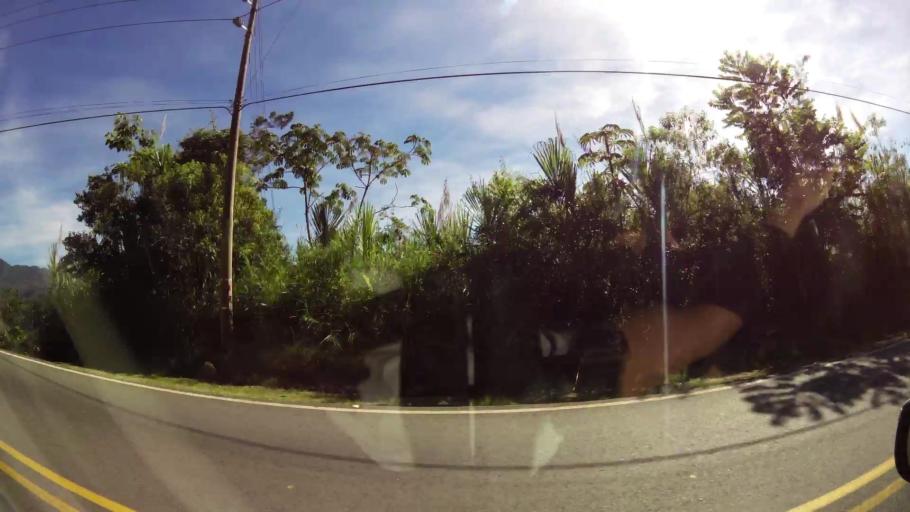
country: CR
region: San Jose
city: San Isidro
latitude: 9.4342
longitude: -83.7095
